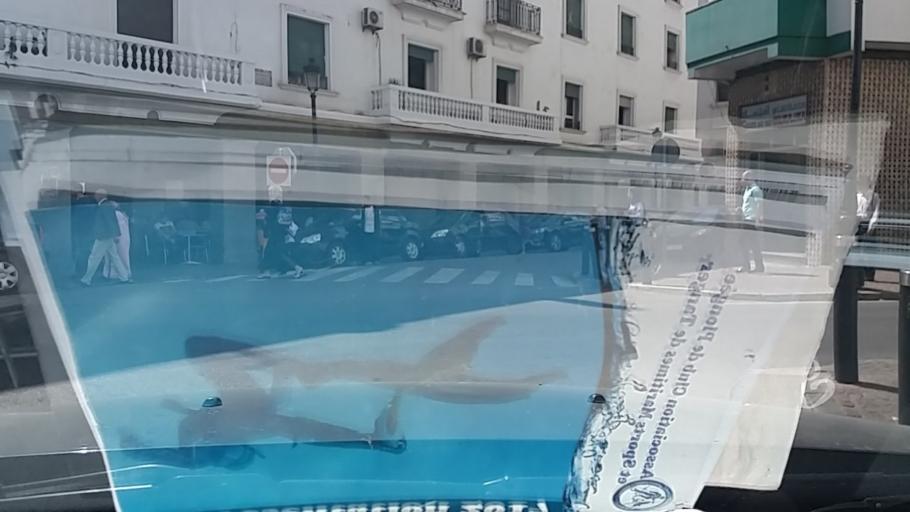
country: MA
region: Tanger-Tetouan
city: Tetouan
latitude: 35.5718
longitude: -5.3767
